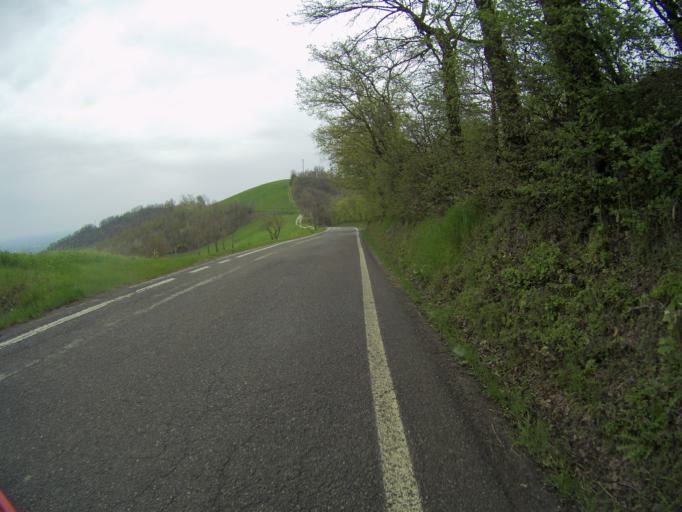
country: IT
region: Emilia-Romagna
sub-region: Provincia di Reggio Emilia
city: San Polo d'Enza
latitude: 44.6107
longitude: 10.4520
